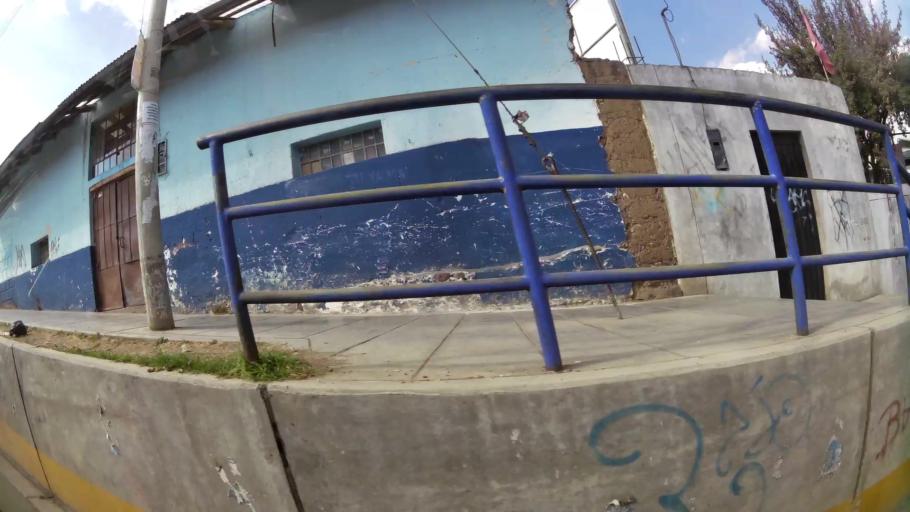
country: PE
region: Junin
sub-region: Provincia de Huancayo
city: El Tambo
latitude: -12.0629
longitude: -75.2114
